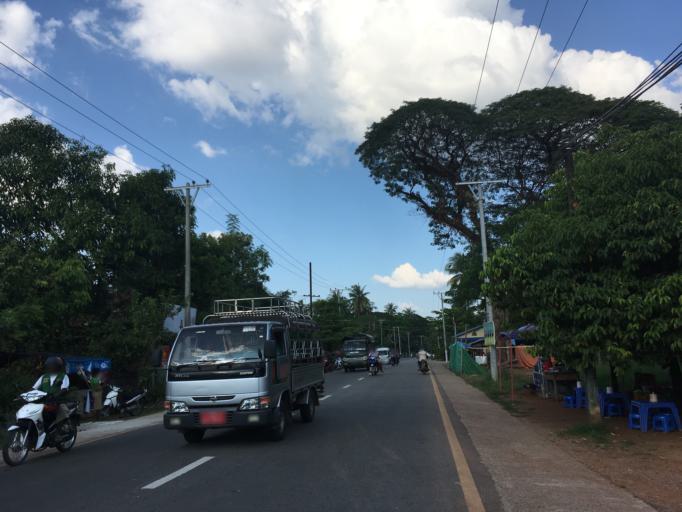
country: MM
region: Mon
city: Mawlamyine
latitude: 16.4448
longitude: 97.6195
